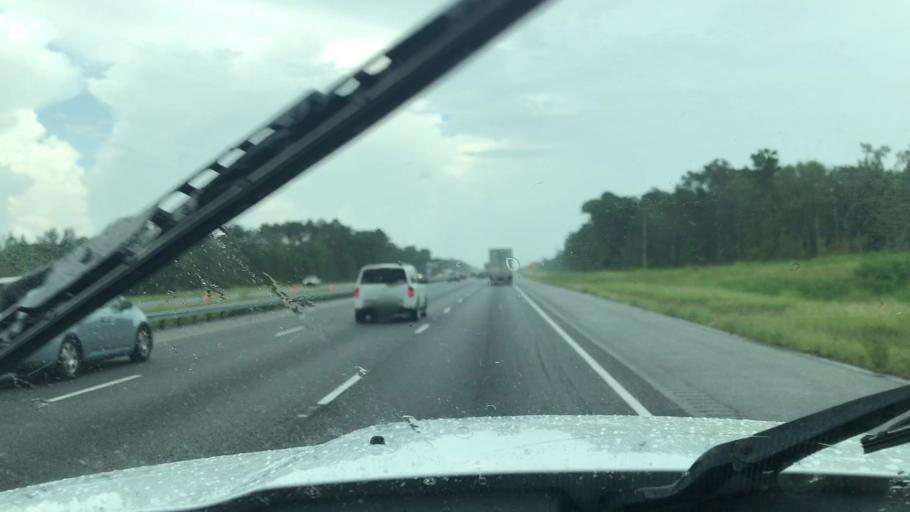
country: US
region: Georgia
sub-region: Camden County
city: Woodbine
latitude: 31.0575
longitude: -81.6382
